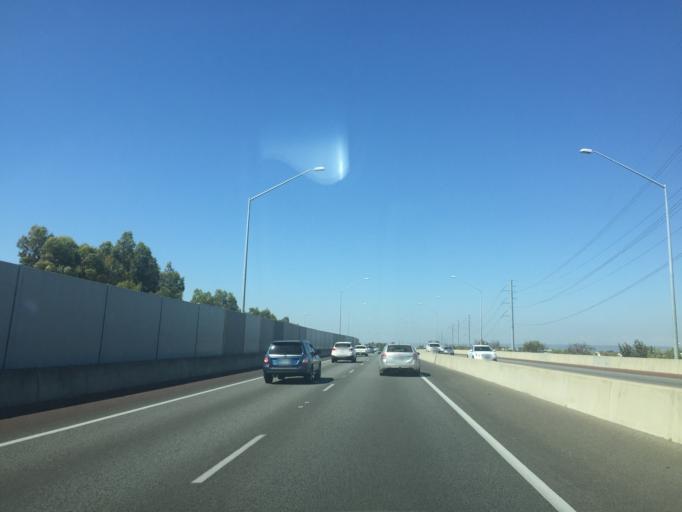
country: AU
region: Western Australia
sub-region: Canning
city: Willetton
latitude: -32.0712
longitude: 115.8879
